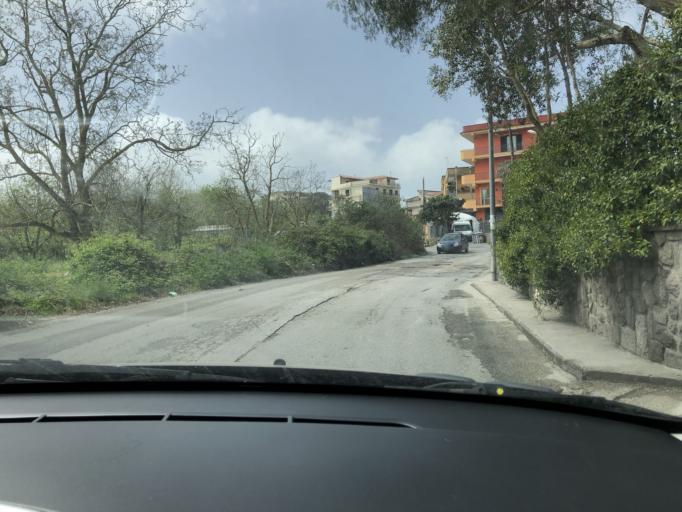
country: IT
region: Campania
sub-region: Provincia di Napoli
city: Torre Caracciolo
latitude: 40.8751
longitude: 14.1850
